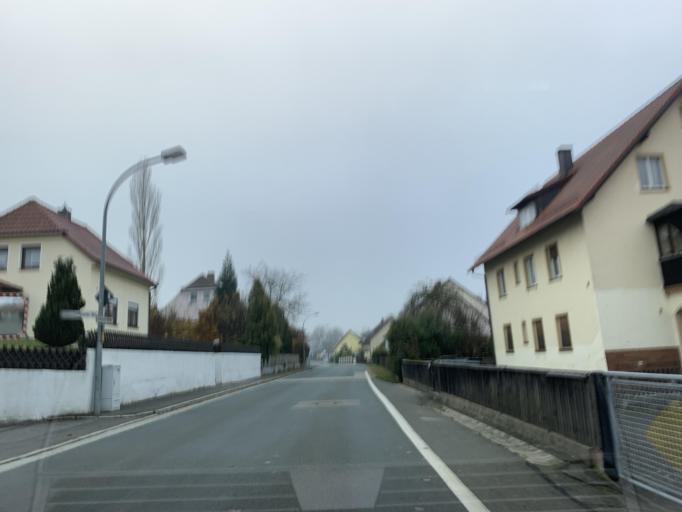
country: DE
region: Bavaria
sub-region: Upper Palatinate
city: Neunburg vorm Wald
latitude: 49.3519
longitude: 12.3900
